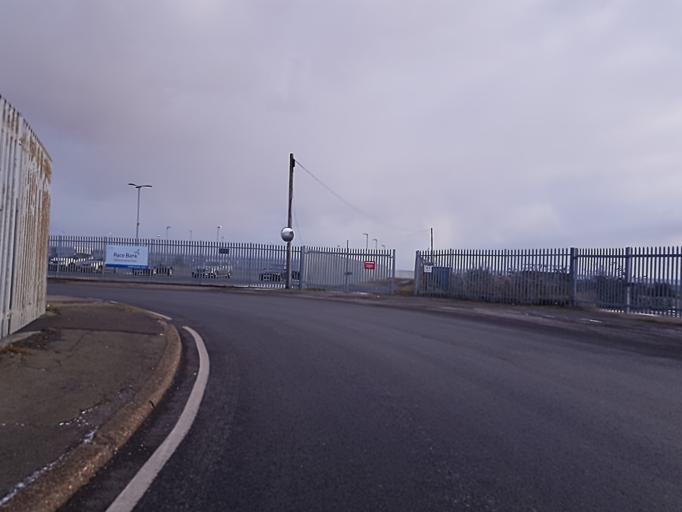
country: GB
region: England
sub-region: North East Lincolnshire
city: Grimsby
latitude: 53.5781
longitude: -0.0573
